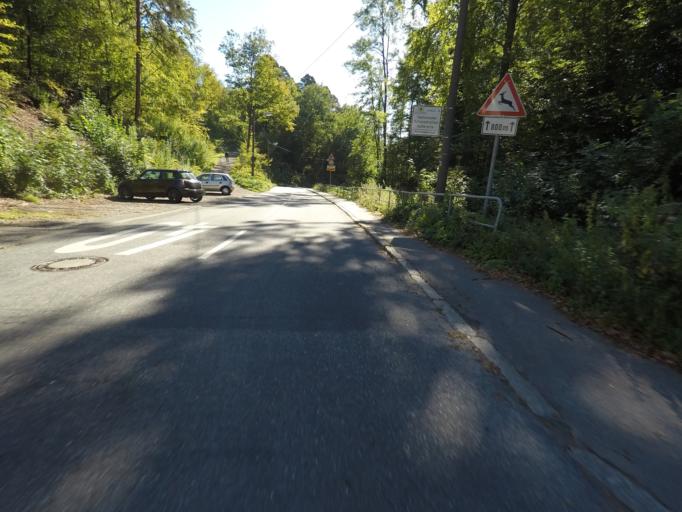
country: DE
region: Baden-Wuerttemberg
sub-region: Regierungsbezirk Stuttgart
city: Stuttgart
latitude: 48.7461
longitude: 9.1221
